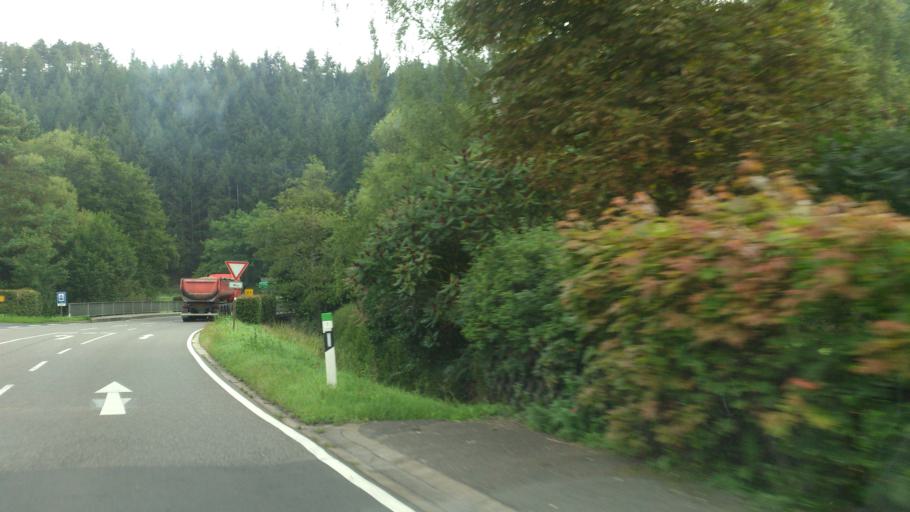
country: DE
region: Rheinland-Pfalz
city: Dorsel
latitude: 50.3696
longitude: 6.7893
